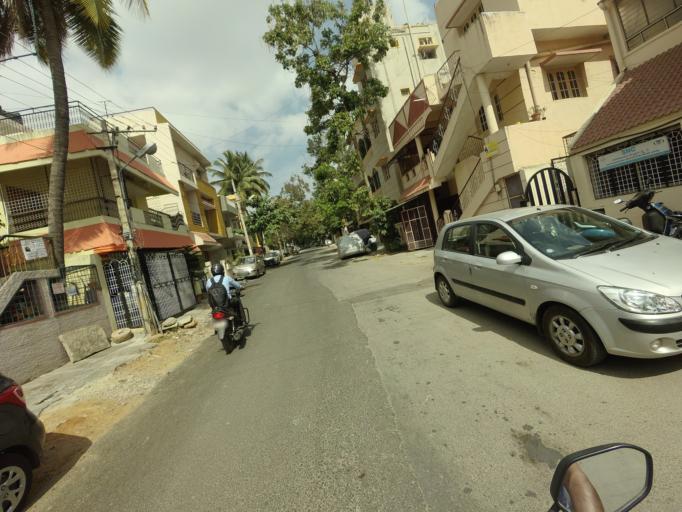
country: IN
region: Karnataka
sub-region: Bangalore Urban
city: Bangalore
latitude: 12.9647
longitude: 77.5358
